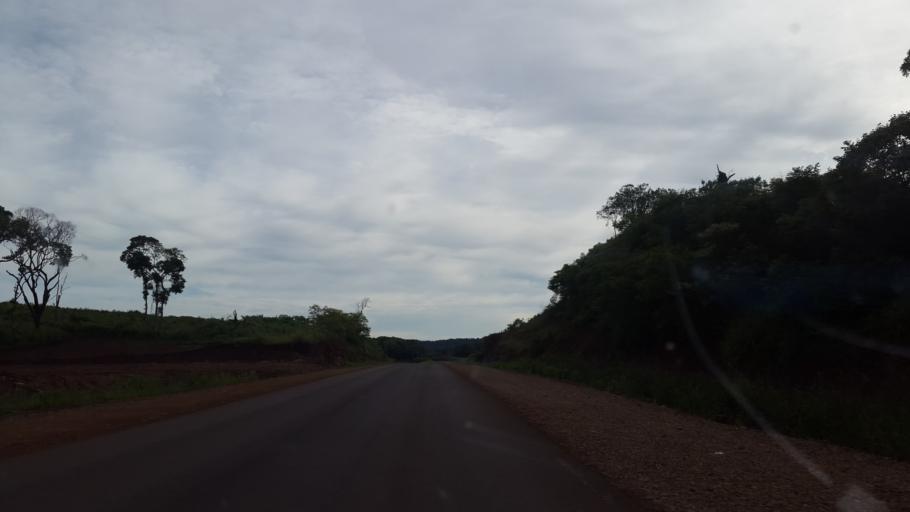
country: AR
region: Misiones
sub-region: Departamento de San Pedro
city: San Pedro
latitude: -26.4798
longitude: -53.8835
